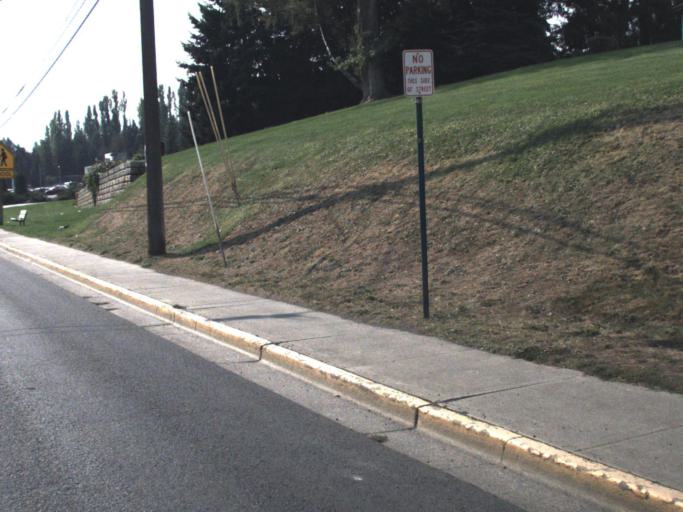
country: US
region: Washington
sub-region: Whitman County
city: Pullman
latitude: 46.7226
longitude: -117.1851
